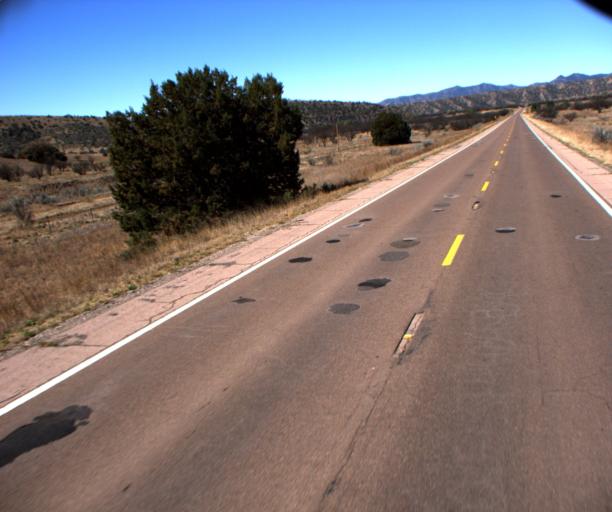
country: US
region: Arizona
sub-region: Pima County
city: Corona de Tucson
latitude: 31.6604
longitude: -110.6905
